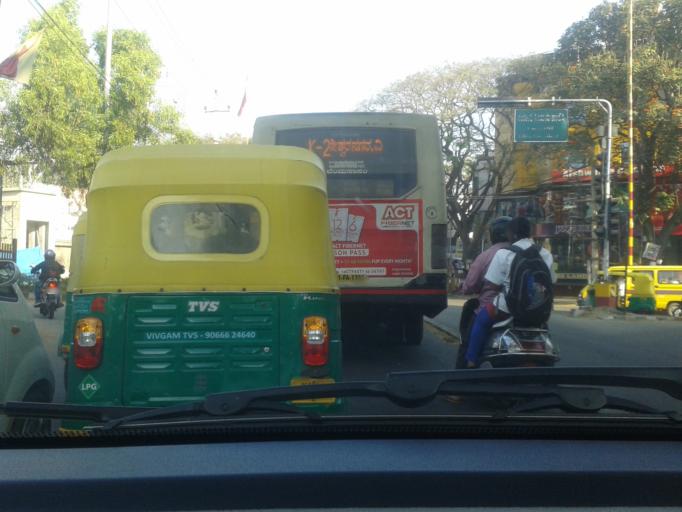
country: IN
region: Karnataka
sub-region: Bangalore Urban
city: Bangalore
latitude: 13.0281
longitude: 77.5714
